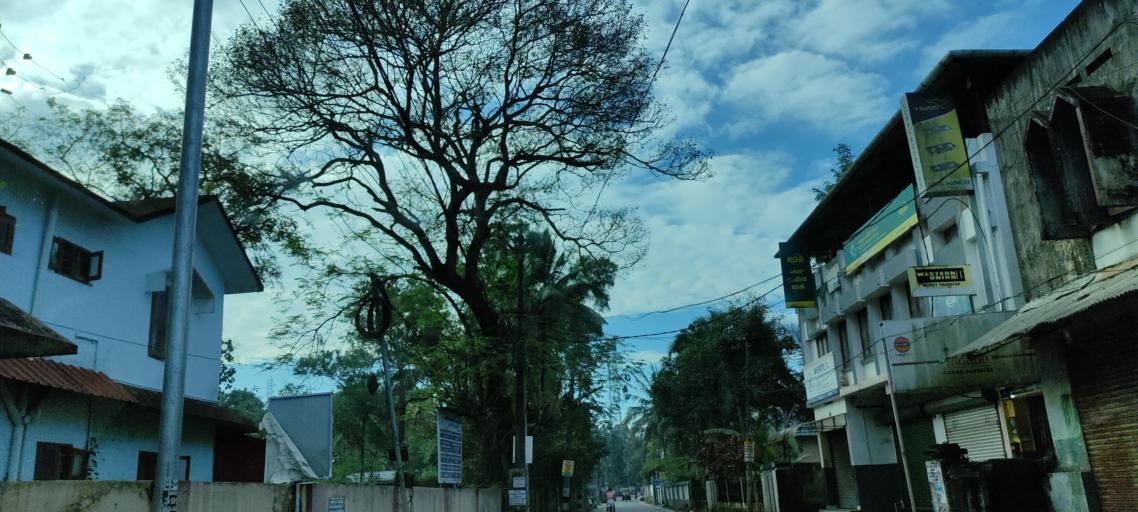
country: IN
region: Kerala
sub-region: Alappuzha
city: Mavelikara
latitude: 9.2529
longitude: 76.5447
